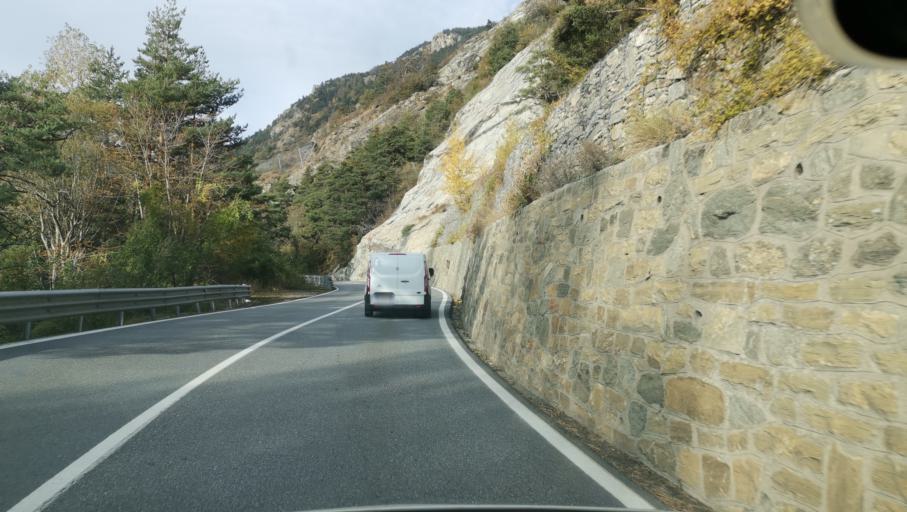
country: IT
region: Piedmont
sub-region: Provincia di Torino
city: Oulx
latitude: 45.0478
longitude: 6.8413
